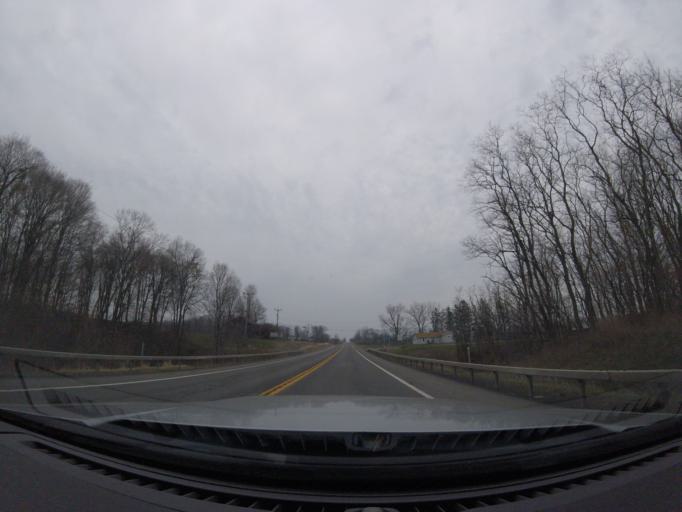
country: US
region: New York
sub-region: Yates County
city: Penn Yan
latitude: 42.6392
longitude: -76.9439
